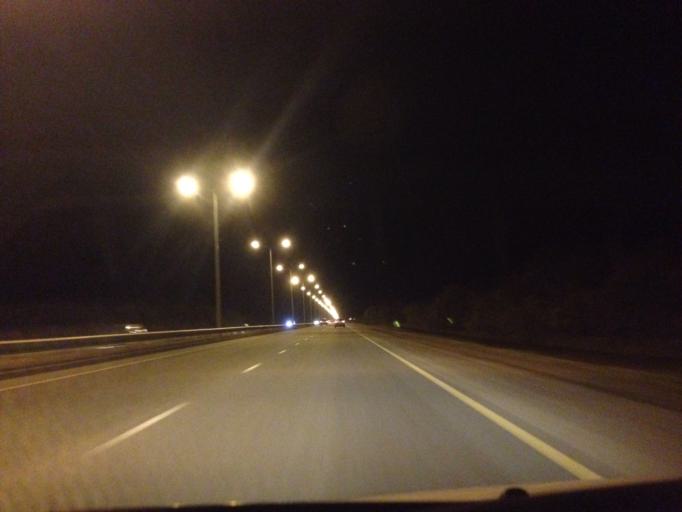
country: KZ
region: Astana Qalasy
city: Astana
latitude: 51.0569
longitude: 71.3908
